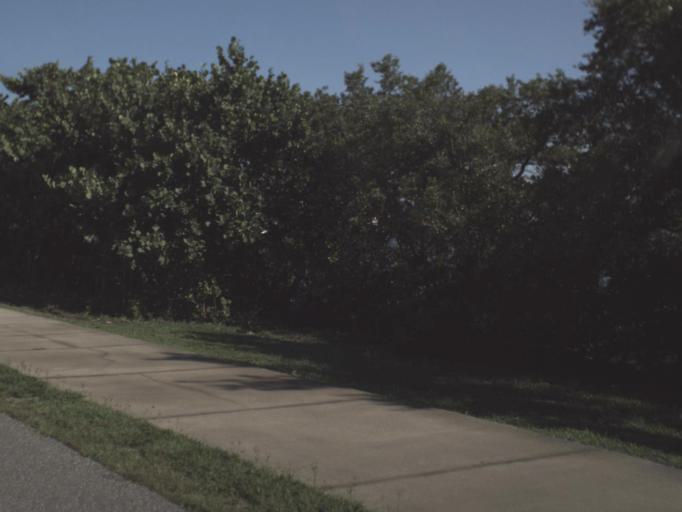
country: US
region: Florida
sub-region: Sarasota County
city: Siesta Key
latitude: 27.3251
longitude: -82.5817
